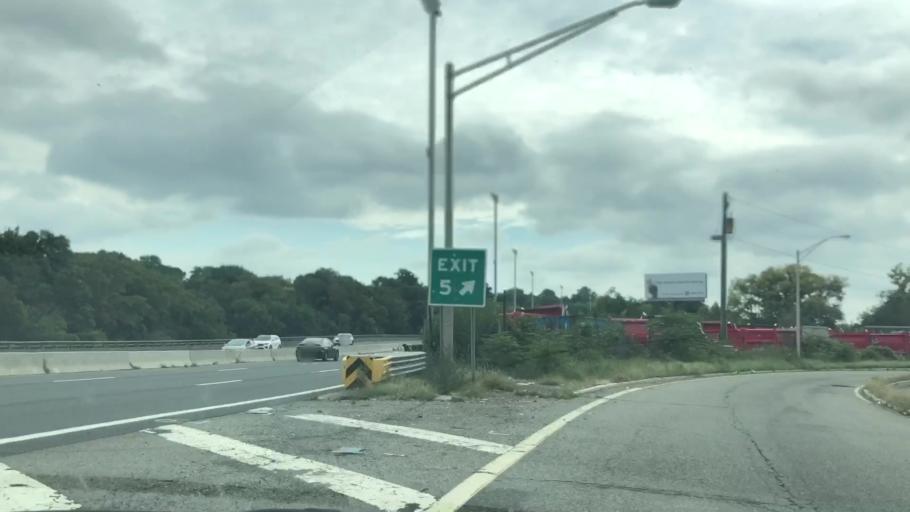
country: US
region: New Jersey
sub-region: Essex County
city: Belleville
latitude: 40.7817
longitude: -74.1493
